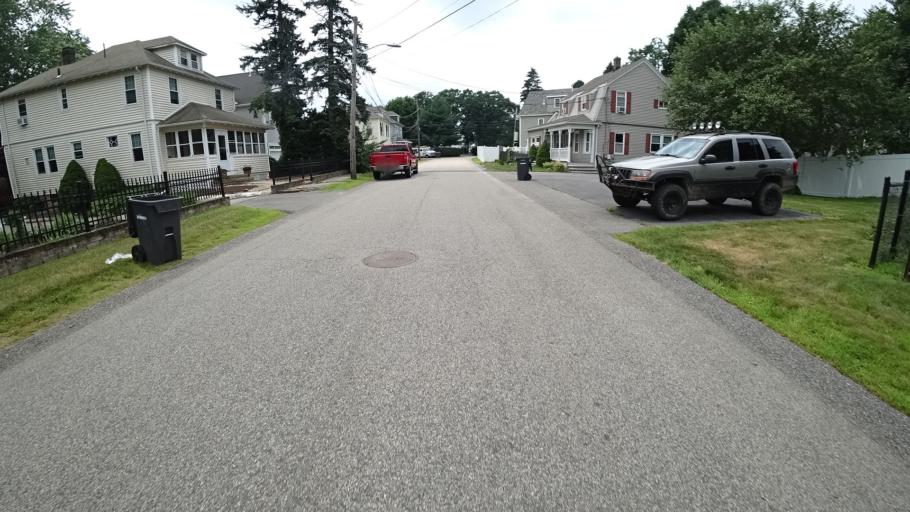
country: US
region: Massachusetts
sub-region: Norfolk County
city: Dedham
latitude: 42.2514
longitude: -71.1575
